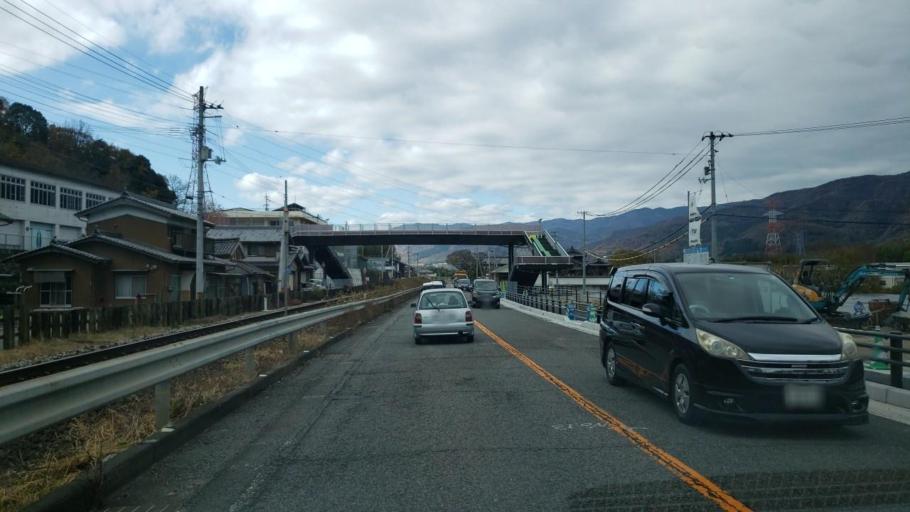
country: JP
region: Tokushima
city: Wakimachi
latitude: 34.0554
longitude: 134.1310
